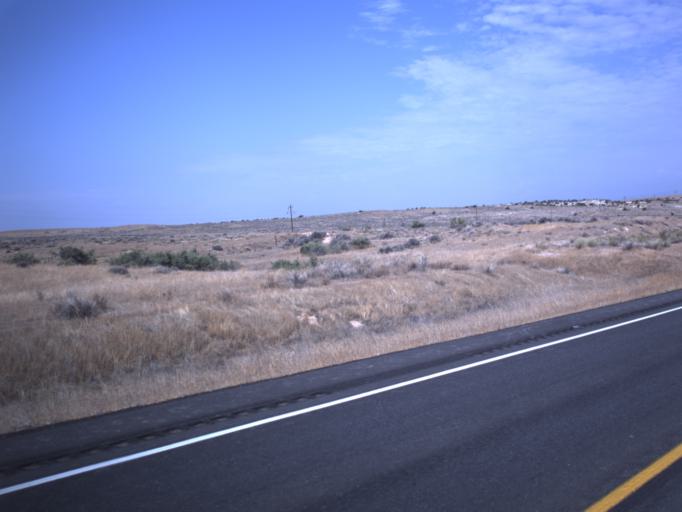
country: US
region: Utah
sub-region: Uintah County
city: Naples
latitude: 40.3415
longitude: -109.2973
